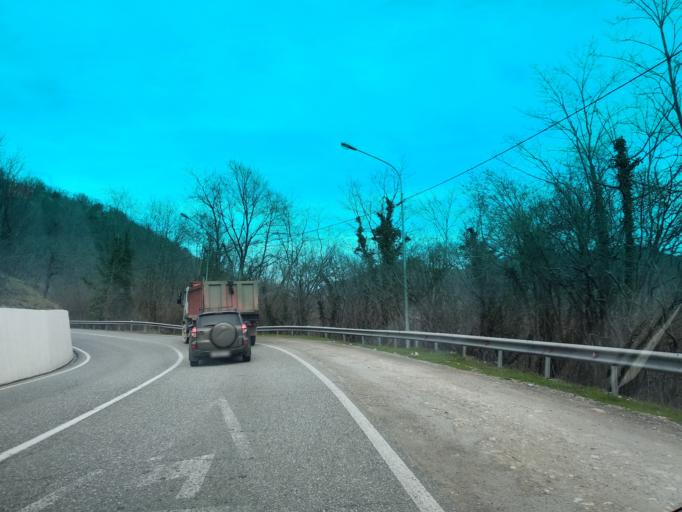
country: RU
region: Krasnodarskiy
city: Shepsi
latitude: 44.0586
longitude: 39.1324
